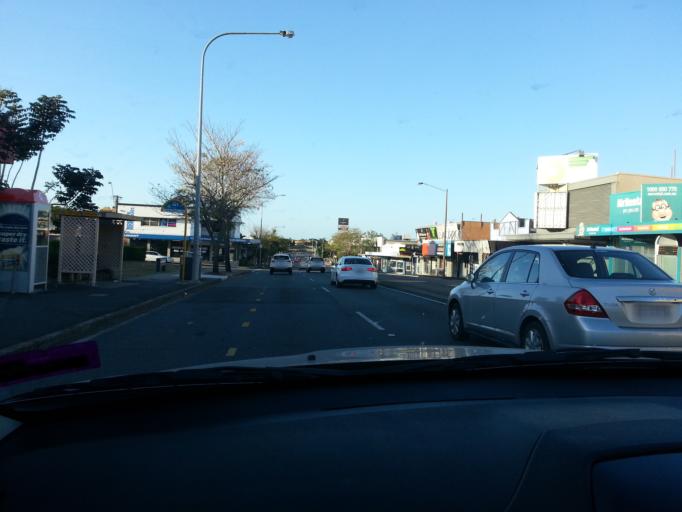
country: AU
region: Queensland
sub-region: Brisbane
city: Wooloowin
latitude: -27.4238
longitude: 153.0336
